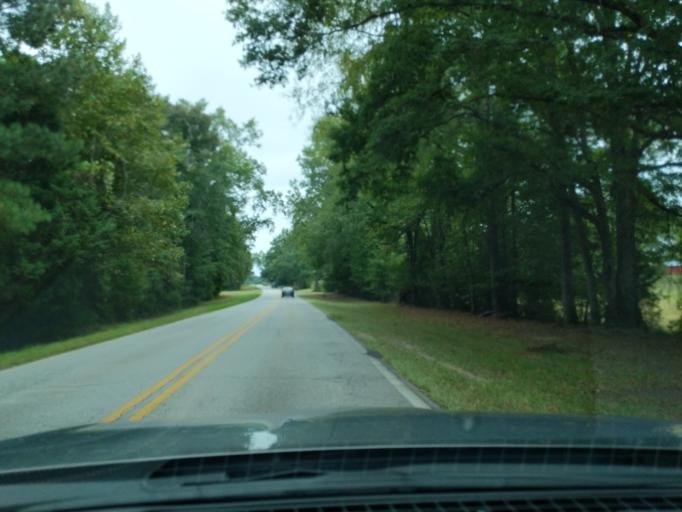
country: US
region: Georgia
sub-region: Columbia County
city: Appling
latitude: 33.6249
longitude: -82.4007
